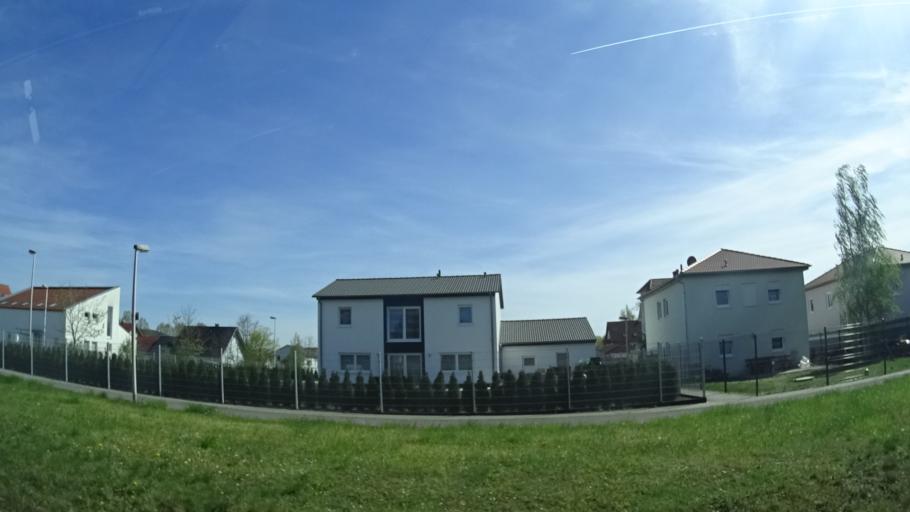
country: DE
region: Bavaria
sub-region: Regierungsbezirk Unterfranken
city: Hofheim in Unterfranken
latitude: 50.1399
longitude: 10.5328
